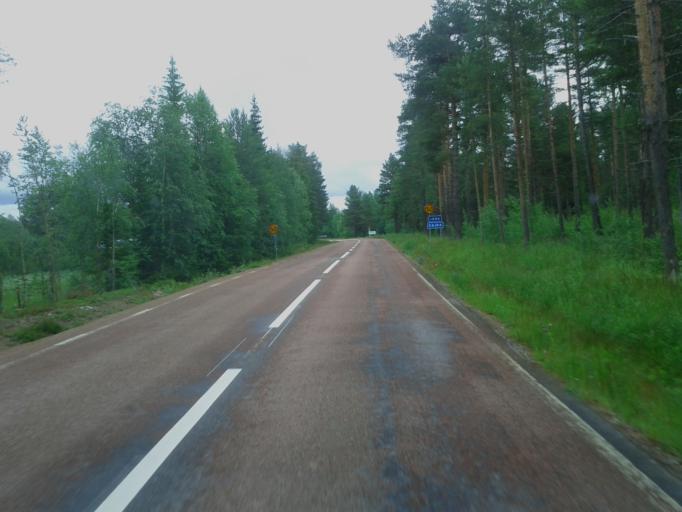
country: NO
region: Hedmark
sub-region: Trysil
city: Innbygda
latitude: 61.8515
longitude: 12.7056
